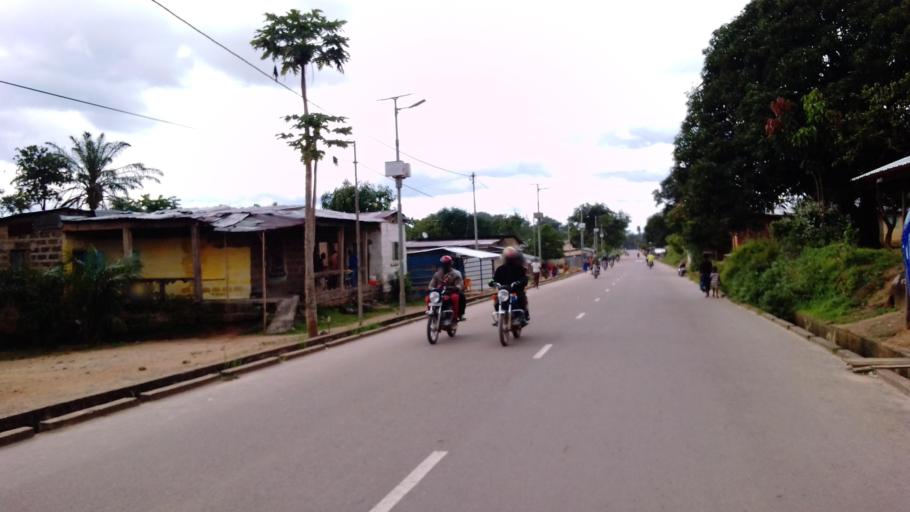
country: SL
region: Eastern Province
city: Koidu
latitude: 8.6527
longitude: -10.9753
